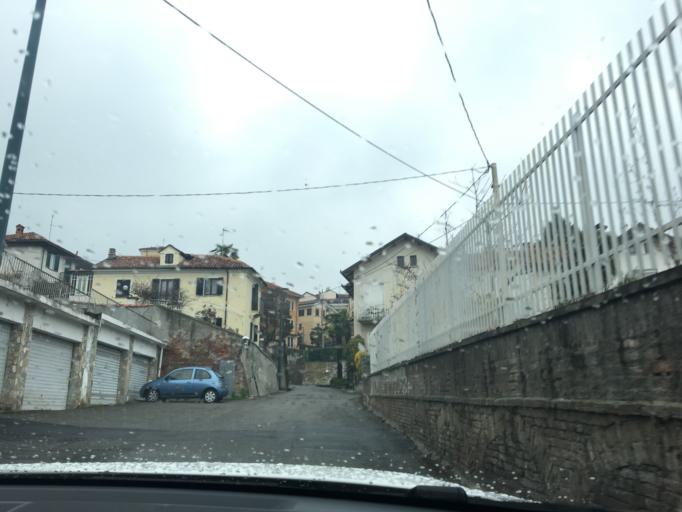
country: IT
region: Piedmont
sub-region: Provincia di Torino
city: Moncalieri
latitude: 45.0279
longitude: 7.6862
